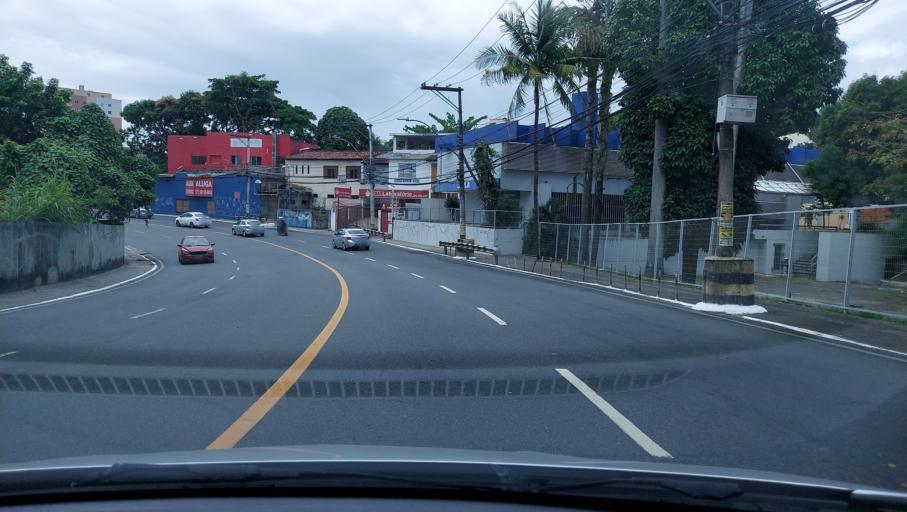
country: BR
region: Bahia
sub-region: Salvador
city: Salvador
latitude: -12.9614
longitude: -38.4691
